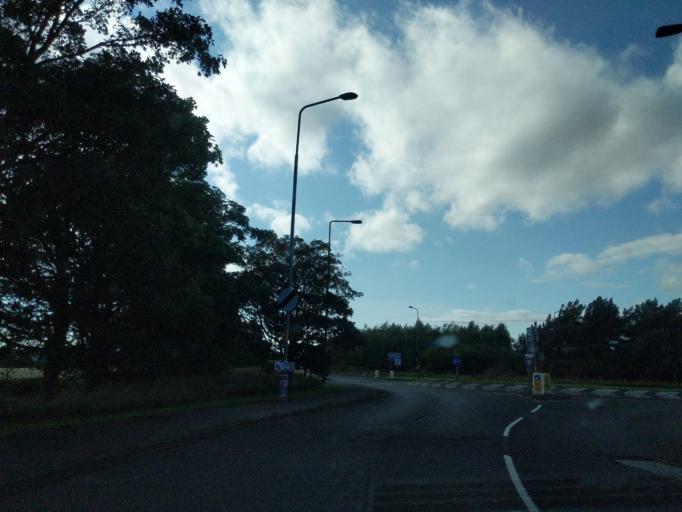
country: GB
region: Scotland
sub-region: East Lothian
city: Haddington
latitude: 55.9542
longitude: -2.8152
